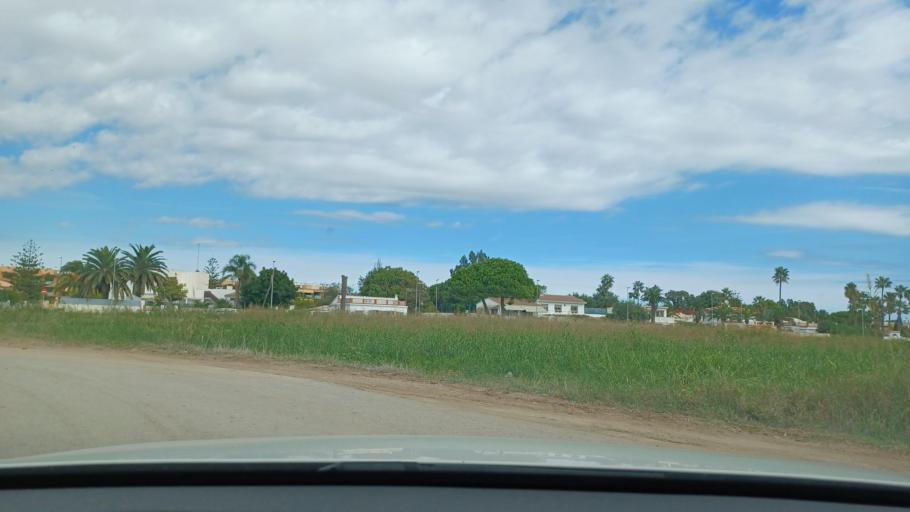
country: ES
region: Catalonia
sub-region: Provincia de Tarragona
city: Deltebre
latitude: 40.6560
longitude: 0.7826
